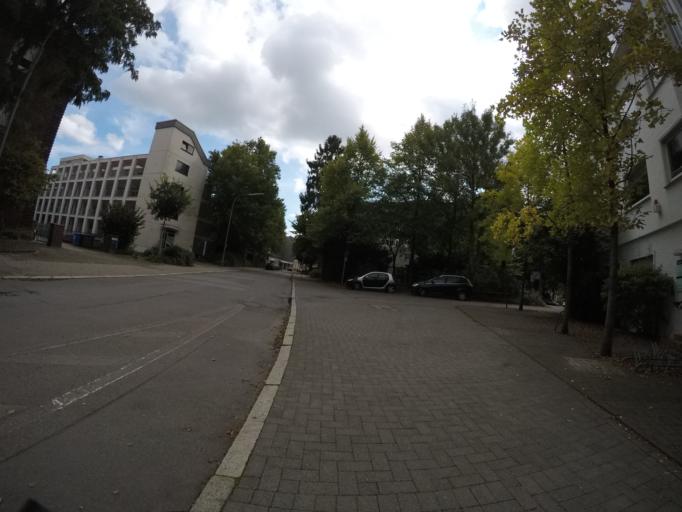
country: DE
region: North Rhine-Westphalia
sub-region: Regierungsbezirk Detmold
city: Herford
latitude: 52.1178
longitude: 8.6696
